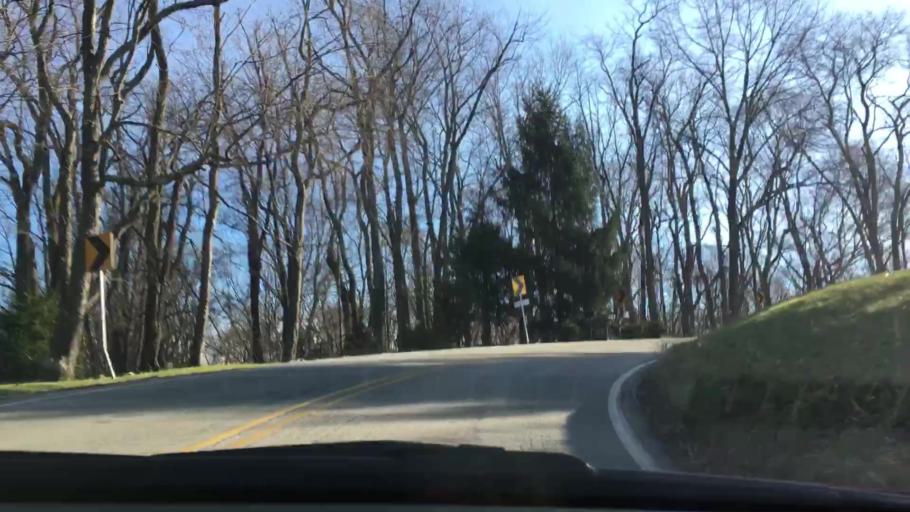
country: US
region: Pennsylvania
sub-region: Westmoreland County
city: Irwin
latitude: 40.3004
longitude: -79.6934
